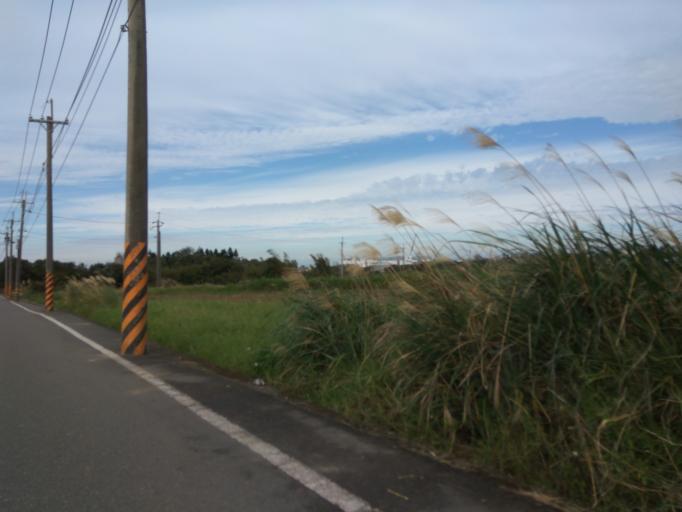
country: TW
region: Taiwan
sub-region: Hsinchu
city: Zhubei
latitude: 24.9598
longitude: 121.1036
